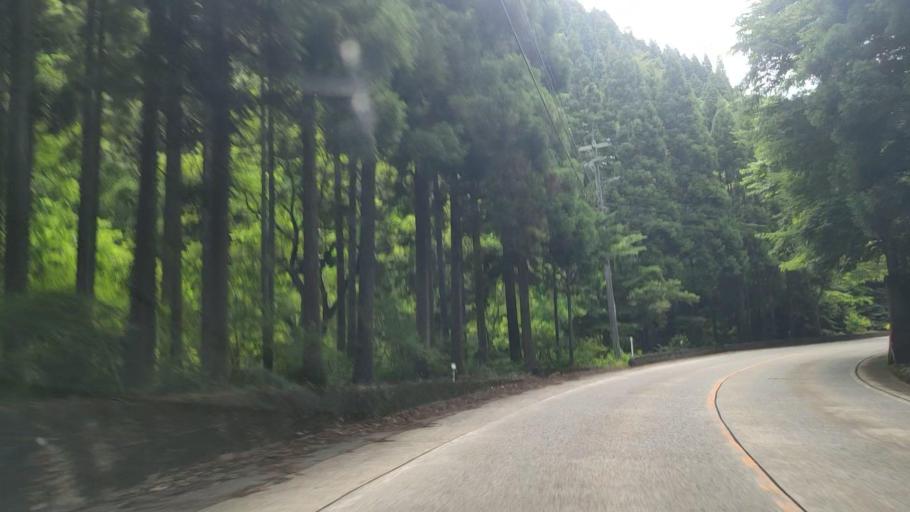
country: JP
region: Okayama
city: Niimi
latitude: 35.2146
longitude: 133.4815
